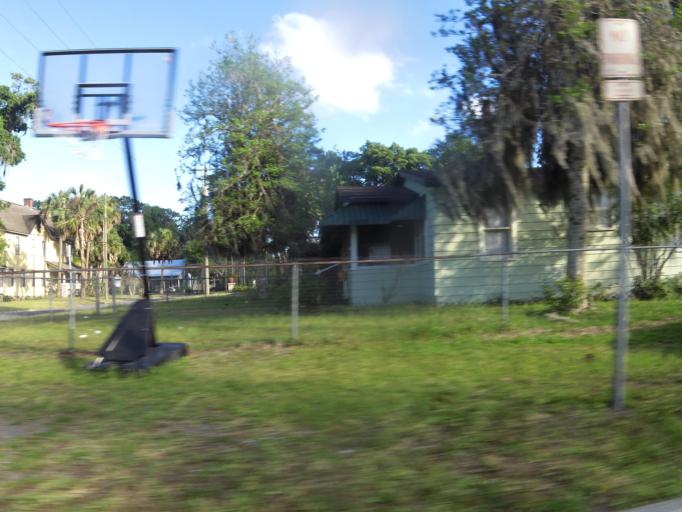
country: US
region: Florida
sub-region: Clay County
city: Green Cove Springs
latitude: 29.9943
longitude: -81.6820
